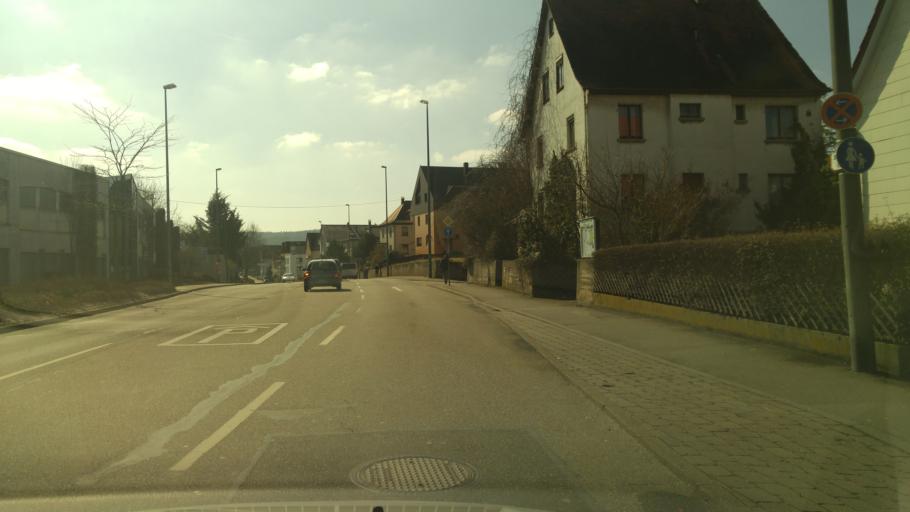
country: DE
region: Baden-Wuerttemberg
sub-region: Regierungsbezirk Stuttgart
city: Leonberg
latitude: 48.7944
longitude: 9.0103
